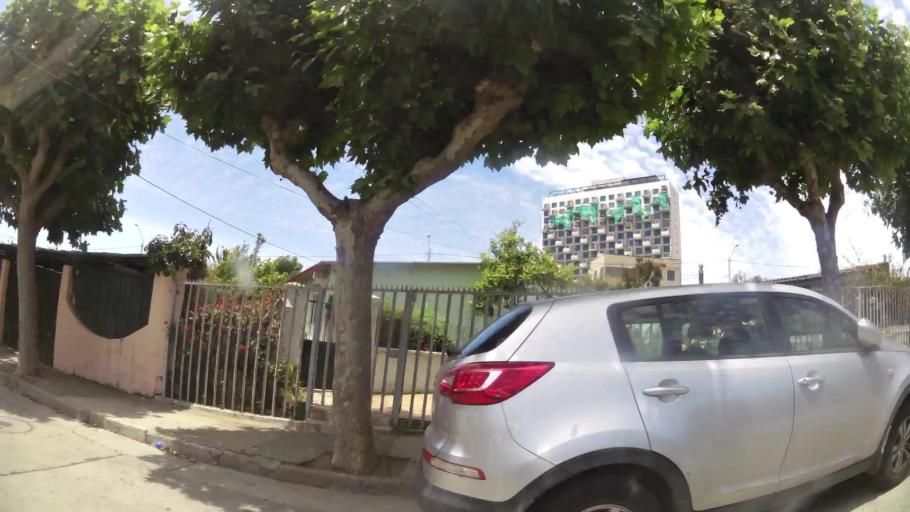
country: CL
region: Valparaiso
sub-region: Provincia de Valparaiso
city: Vina del Mar
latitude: -33.0480
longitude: -71.5760
